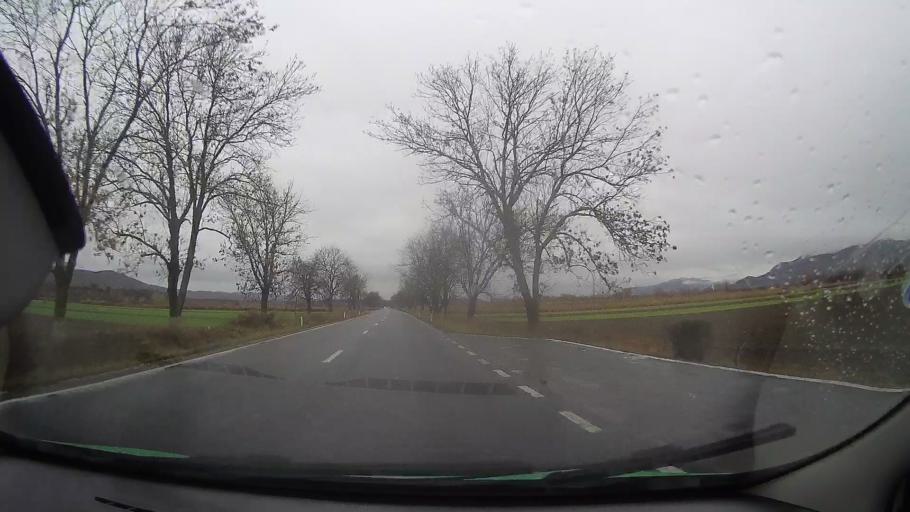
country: RO
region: Mures
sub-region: Comuna Suseni
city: Suseni
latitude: 46.8304
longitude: 24.7414
